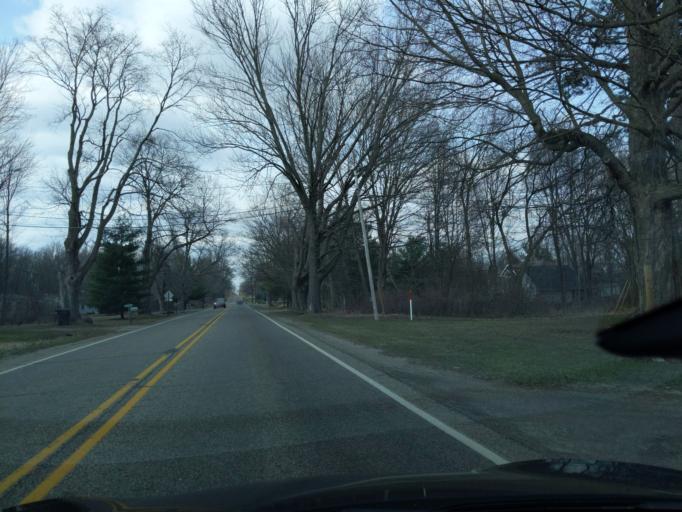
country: US
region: Michigan
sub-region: Jackson County
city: Jackson
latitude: 42.3111
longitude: -84.4136
